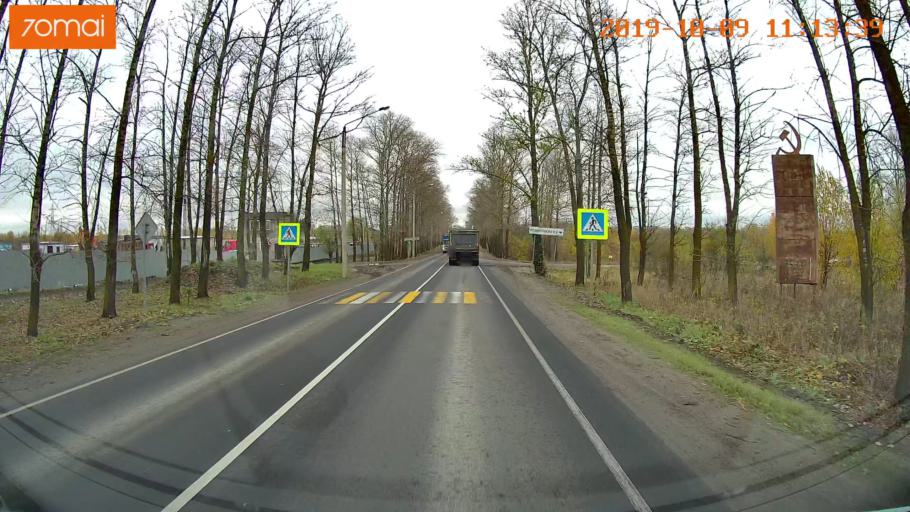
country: RU
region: Vologda
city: Vologda
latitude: 59.1833
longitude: 39.8454
